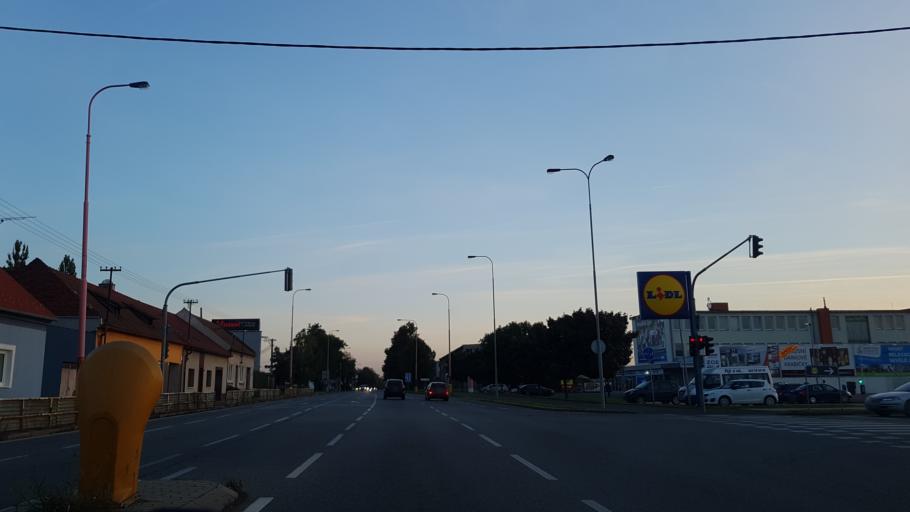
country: CZ
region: Zlin
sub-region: Okres Uherske Hradiste
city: Uherske Hradiste
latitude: 49.0587
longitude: 17.4665
